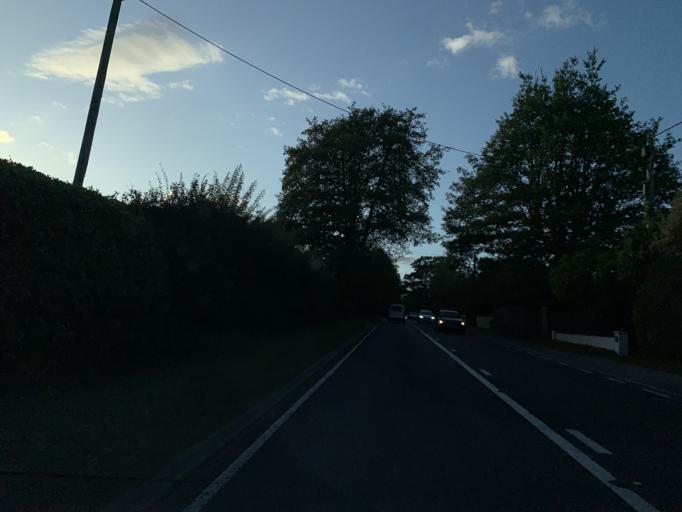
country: GB
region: England
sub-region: Hampshire
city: West Wellow
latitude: 50.9643
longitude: -1.5706
